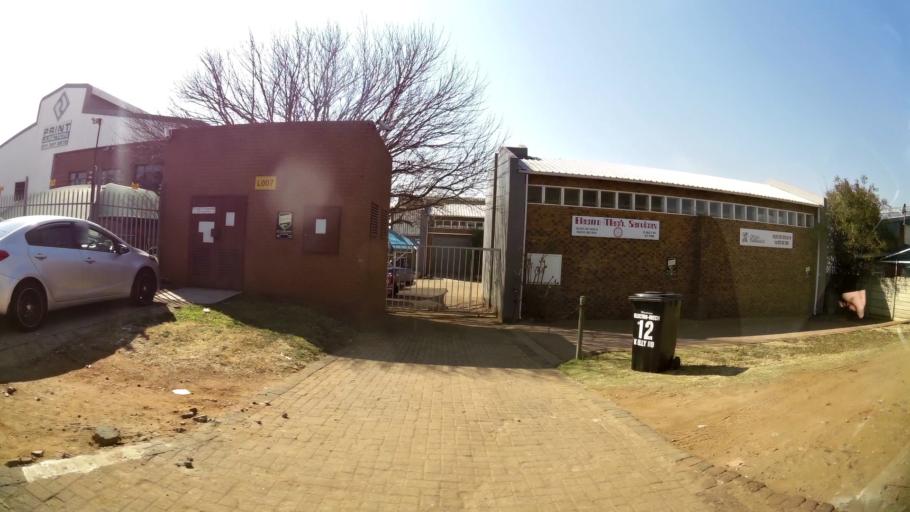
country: ZA
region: Gauteng
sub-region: Ekurhuleni Metropolitan Municipality
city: Boksburg
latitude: -26.1702
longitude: 28.2276
